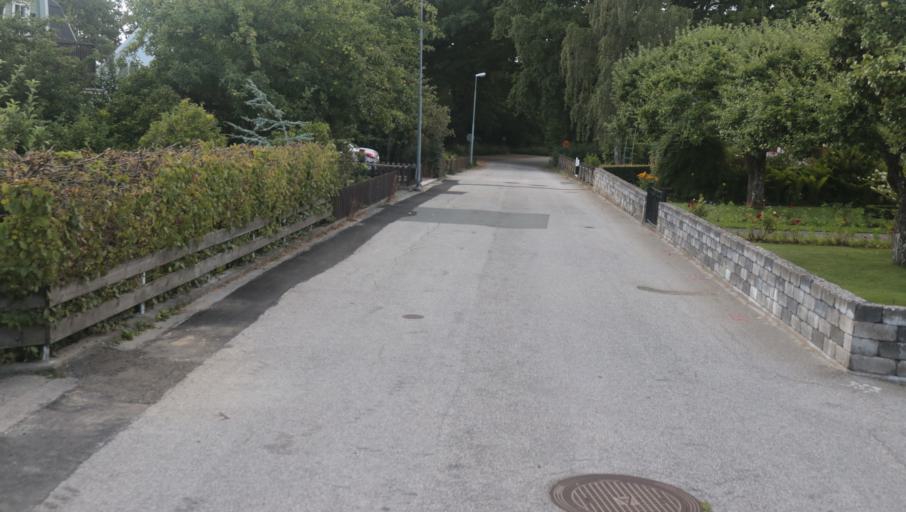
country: SE
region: Blekinge
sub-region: Karlshamns Kommun
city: Morrum
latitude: 56.1900
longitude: 14.7482
